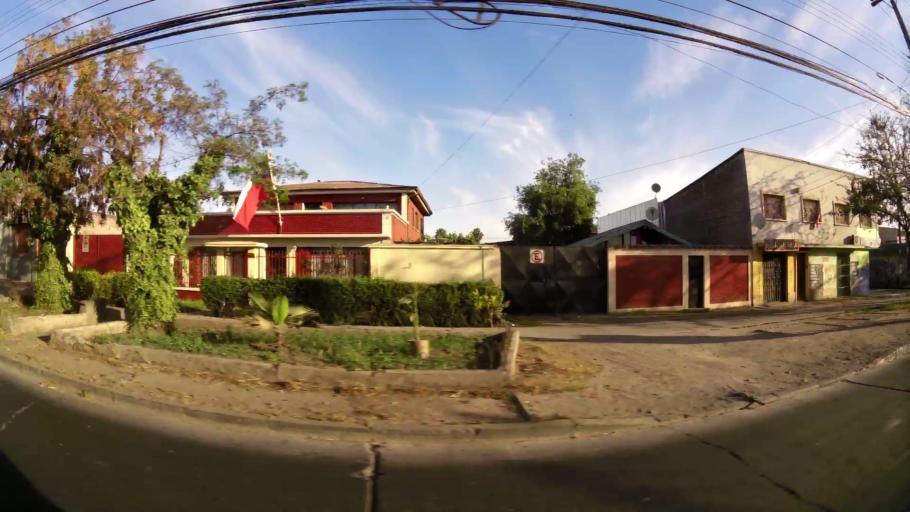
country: CL
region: Santiago Metropolitan
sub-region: Provincia de Santiago
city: Lo Prado
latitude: -33.4431
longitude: -70.7143
